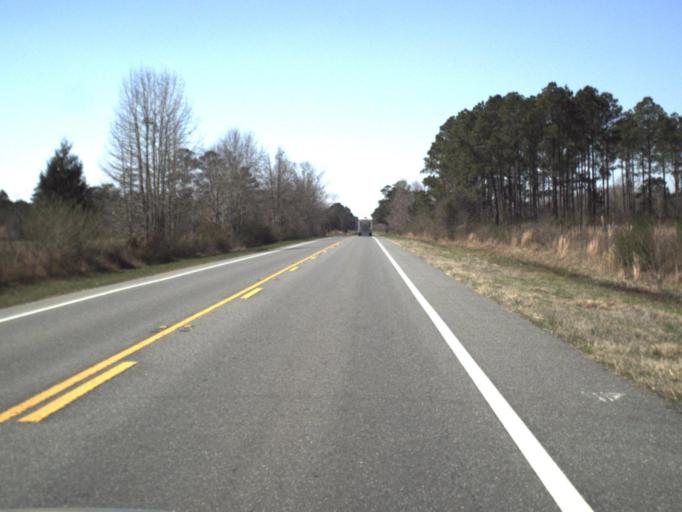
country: US
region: Florida
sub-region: Washington County
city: Chipley
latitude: 30.7892
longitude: -85.4161
